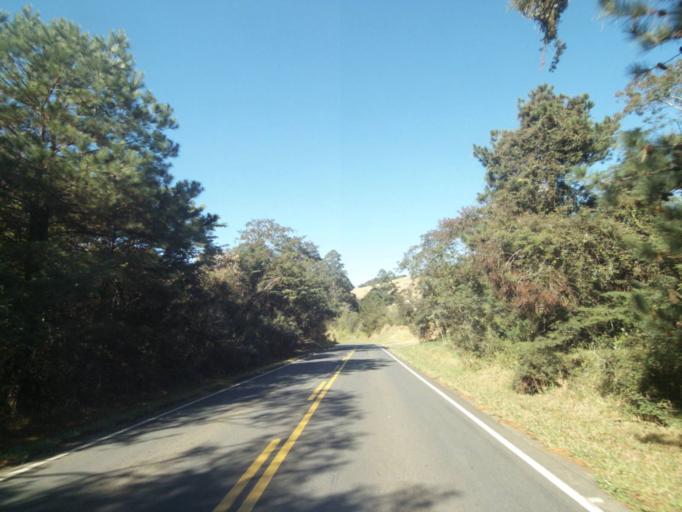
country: BR
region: Parana
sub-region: Tibagi
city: Tibagi
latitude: -24.4681
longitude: -50.5382
